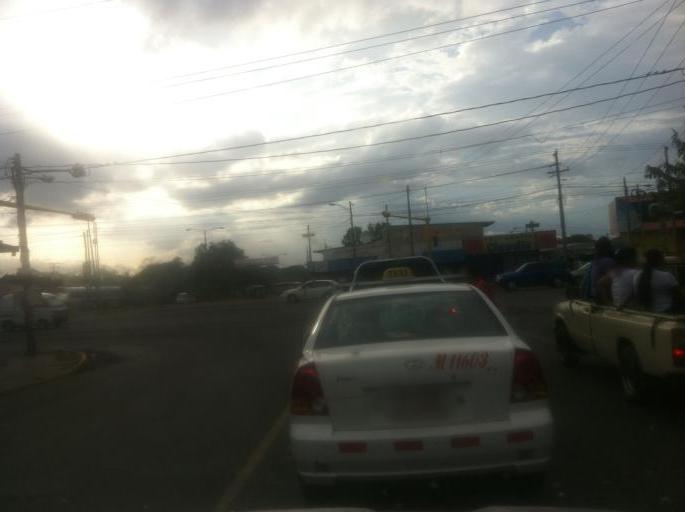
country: NI
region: Managua
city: Managua
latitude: 12.1220
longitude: -86.2437
